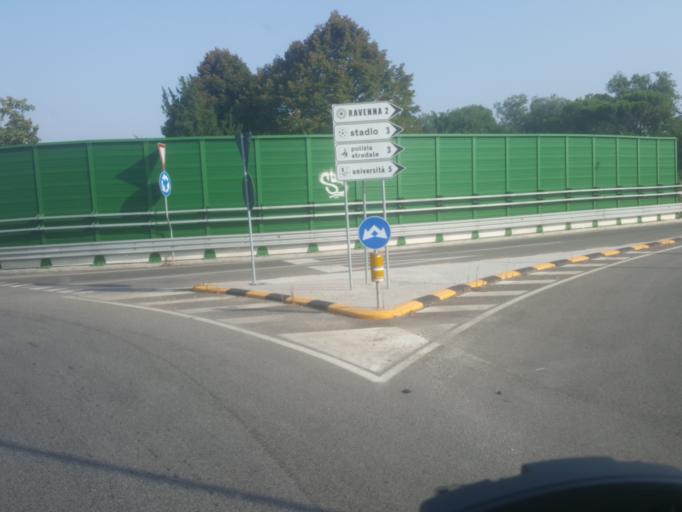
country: IT
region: Emilia-Romagna
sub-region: Provincia di Ravenna
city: Madonna Dell'Albero
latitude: 44.3845
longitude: 12.1951
